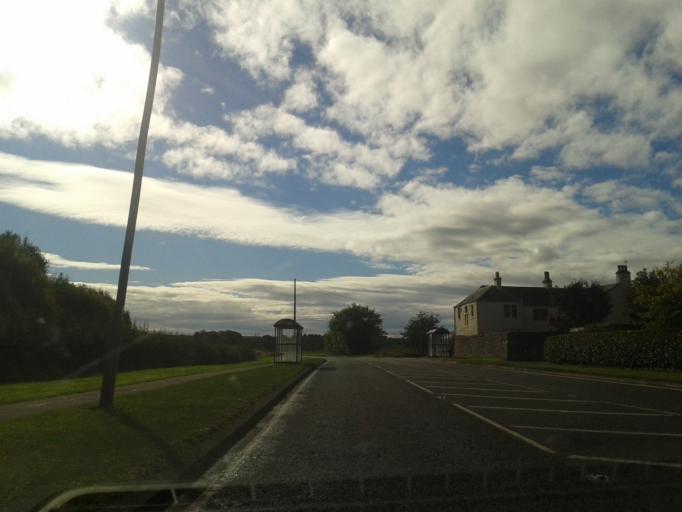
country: GB
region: Scotland
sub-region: Fife
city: Newport-On-Tay
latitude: 56.4153
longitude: -2.9175
